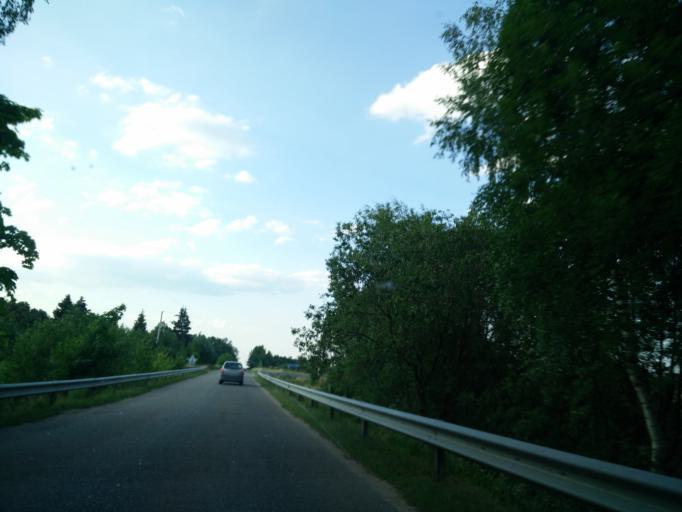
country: LT
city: Trakai
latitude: 54.6867
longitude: 24.9577
